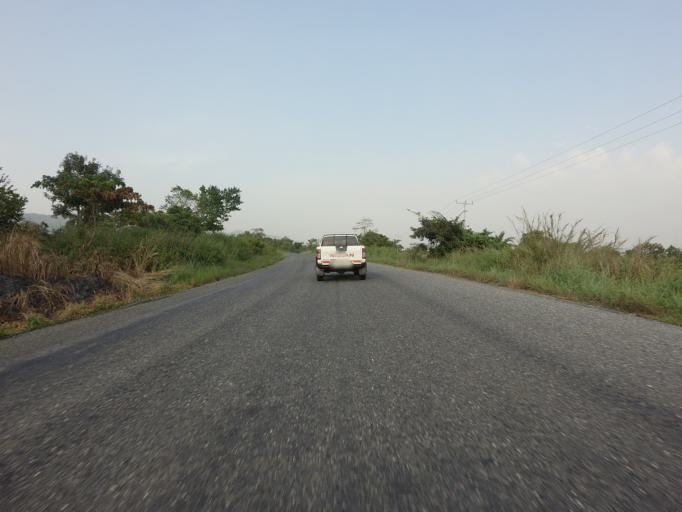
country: GH
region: Volta
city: Ho
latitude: 6.4683
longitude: 0.2252
